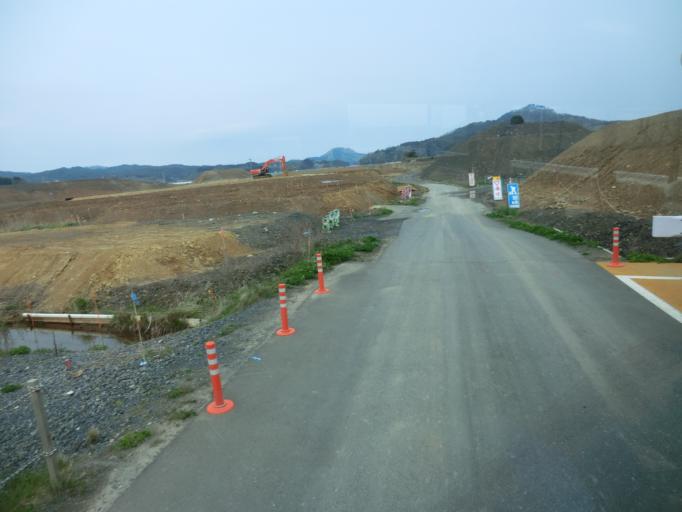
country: JP
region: Iwate
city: Ofunato
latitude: 38.8694
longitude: 141.5845
